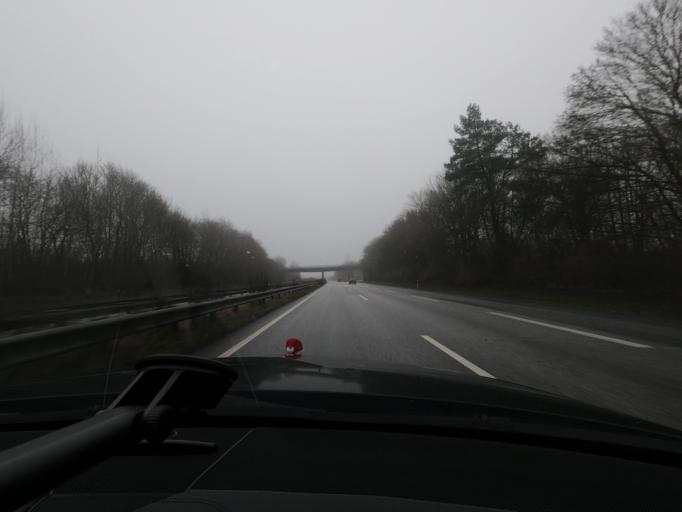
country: DE
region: Schleswig-Holstein
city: Husby
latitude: 54.5073
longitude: 9.5020
